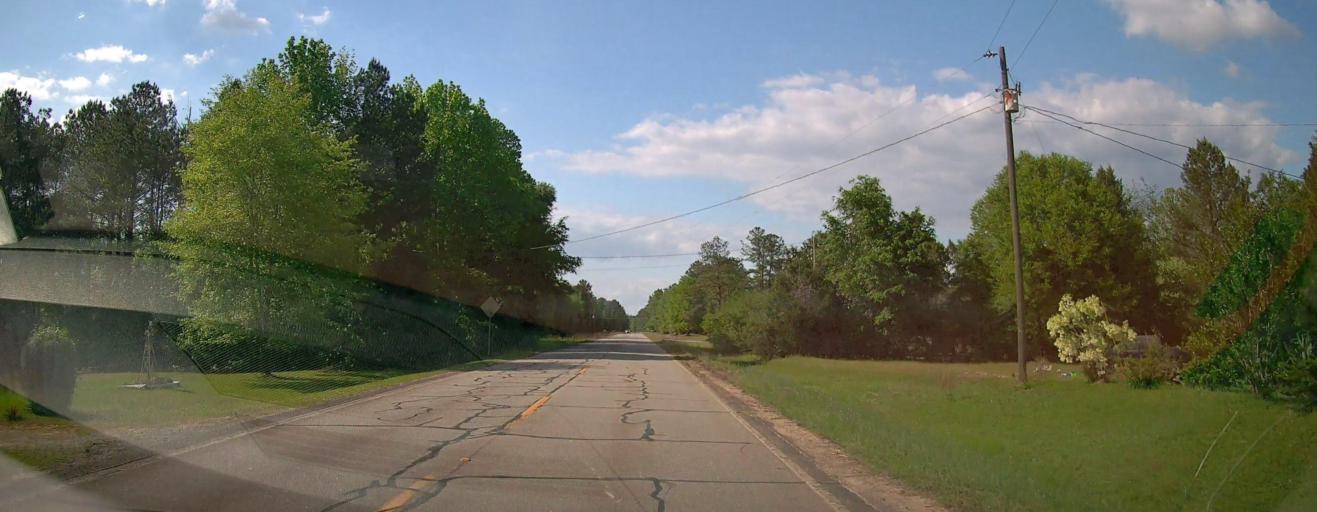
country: US
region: Georgia
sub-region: Washington County
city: Tennille
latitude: 32.8974
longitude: -82.9673
